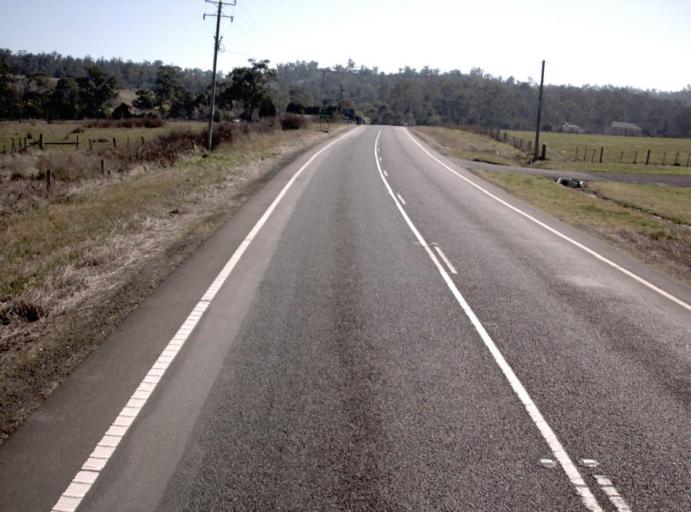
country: AU
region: Tasmania
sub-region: Launceston
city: Mayfield
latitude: -41.3135
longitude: 147.0530
